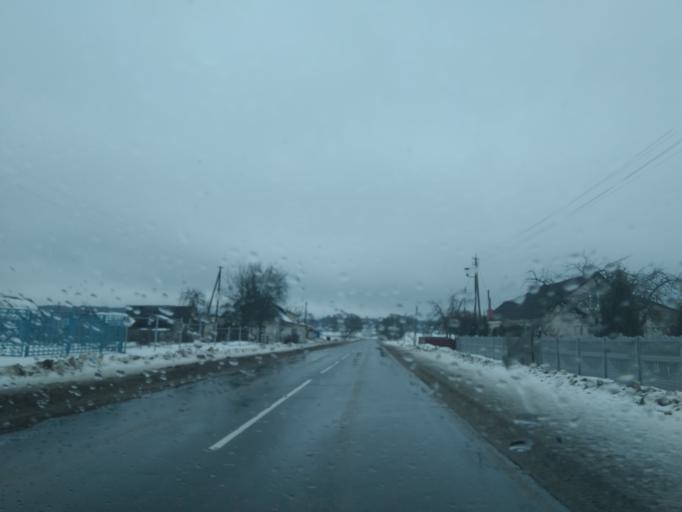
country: BY
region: Minsk
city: Stowbtsy
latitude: 53.5820
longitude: 26.8324
